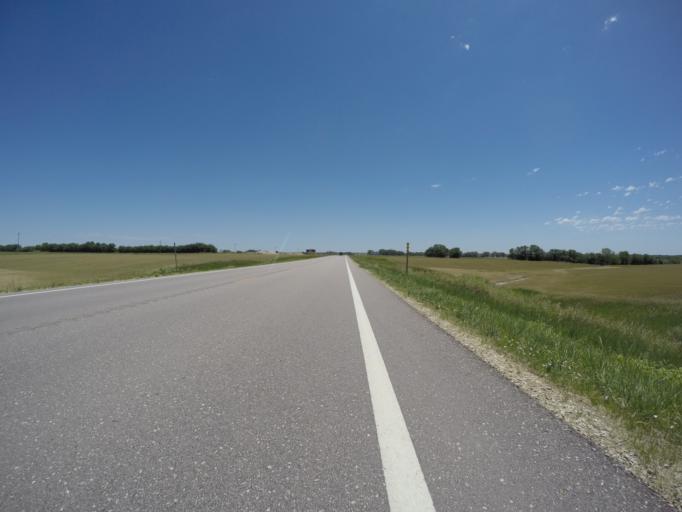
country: US
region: Kansas
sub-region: Republic County
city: Belleville
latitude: 39.8119
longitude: -97.7014
